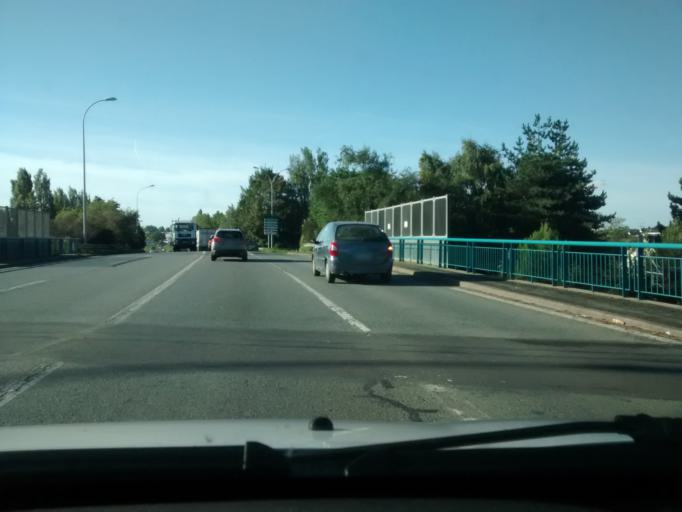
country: FR
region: Brittany
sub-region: Departement d'Ille-et-Vilaine
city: Saint-Malo
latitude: 48.6441
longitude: -1.9904
